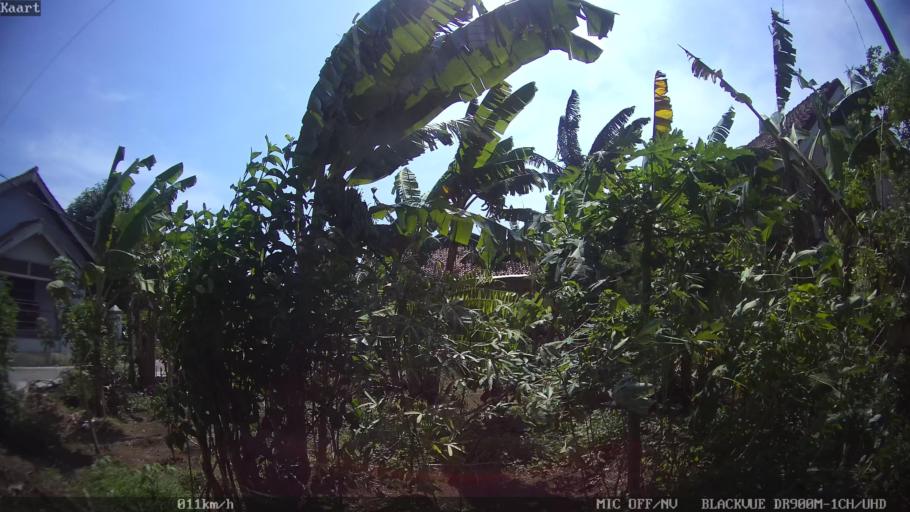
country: ID
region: Lampung
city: Kedaton
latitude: -5.3635
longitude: 105.2544
